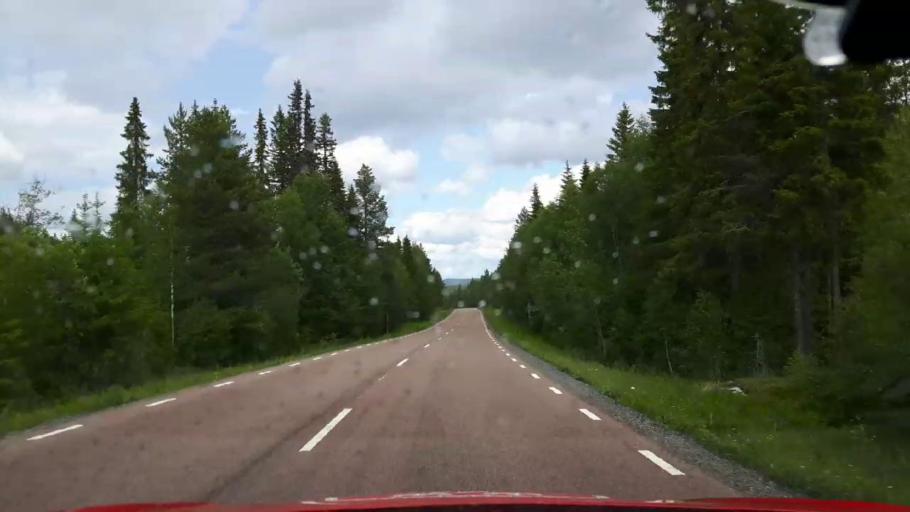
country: SE
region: Jaemtland
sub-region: Krokoms Kommun
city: Valla
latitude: 63.9396
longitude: 14.2219
